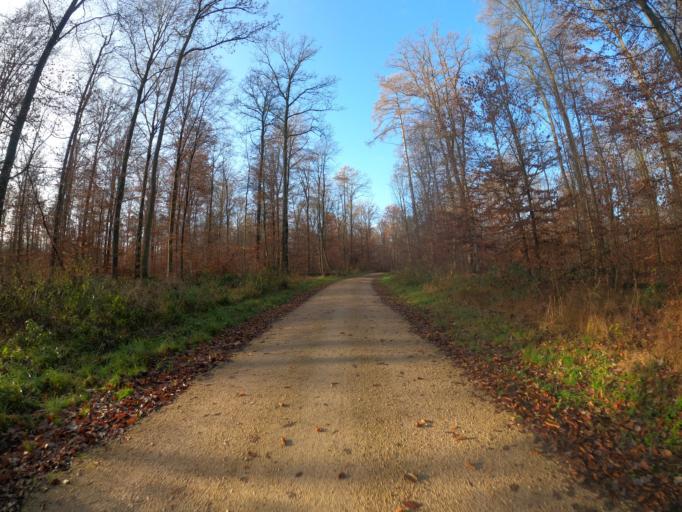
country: DE
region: Baden-Wuerttemberg
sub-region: Regierungsbezirk Stuttgart
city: Schlierbach
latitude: 48.6711
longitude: 9.5437
